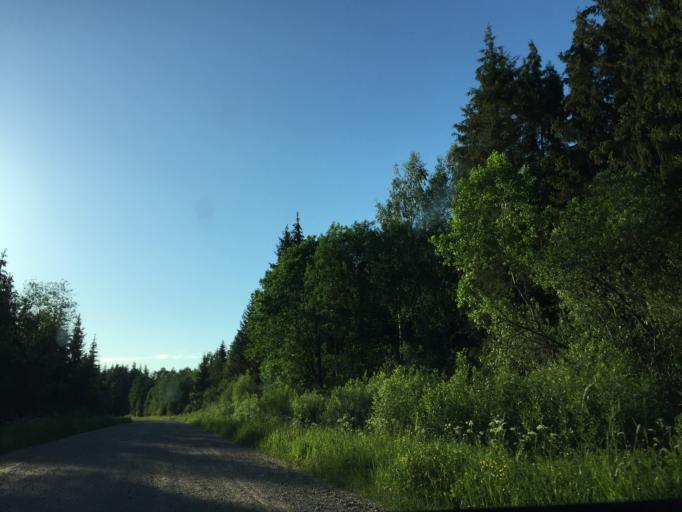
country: LV
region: Talsu Rajons
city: Sabile
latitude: 56.8688
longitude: 22.6365
